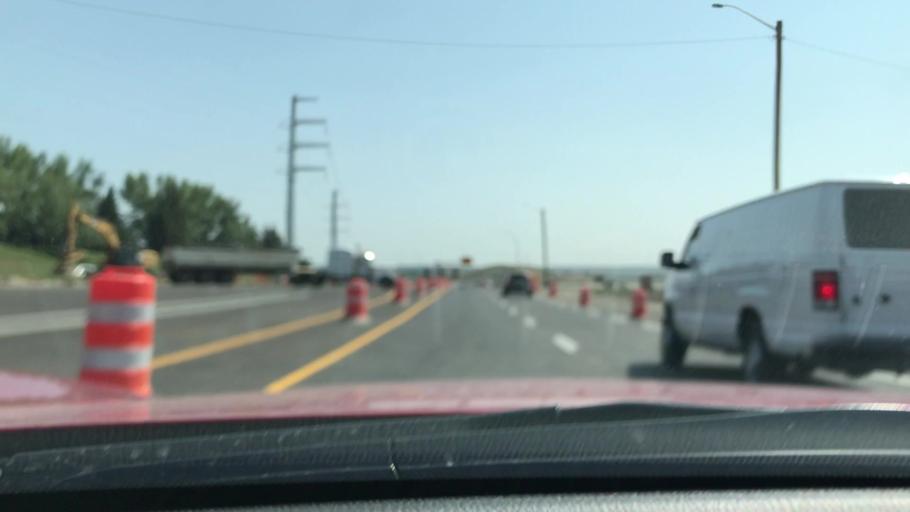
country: CA
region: Alberta
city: Calgary
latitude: 51.0127
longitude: -114.1653
